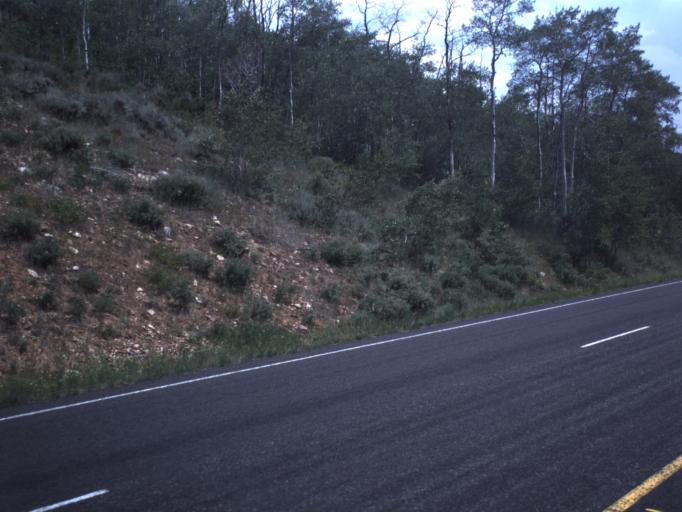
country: US
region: Utah
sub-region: Summit County
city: Francis
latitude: 40.4780
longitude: -110.9391
